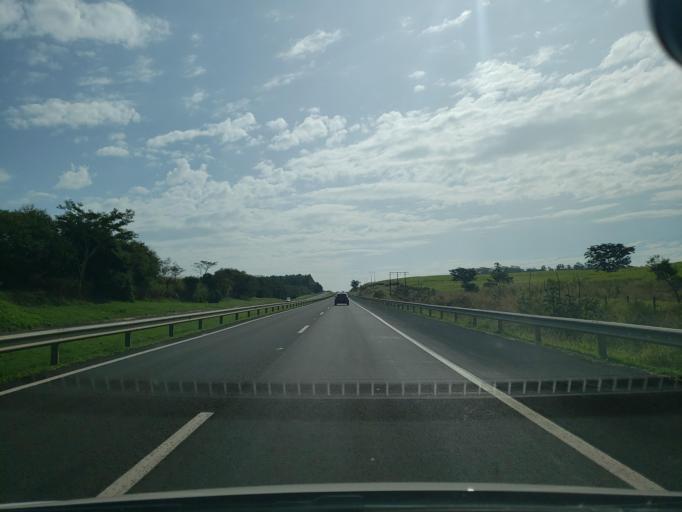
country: BR
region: Sao Paulo
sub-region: Lins
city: Lins
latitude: -21.7283
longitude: -49.7137
